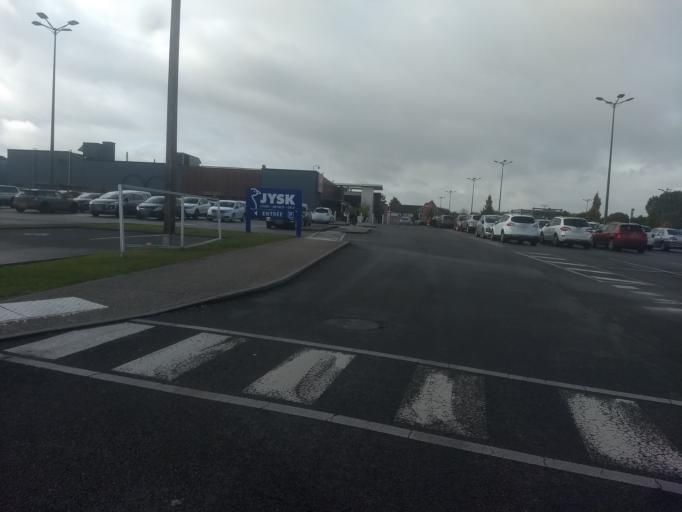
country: FR
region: Nord-Pas-de-Calais
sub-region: Departement du Pas-de-Calais
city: Dainville
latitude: 50.2827
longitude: 2.7407
